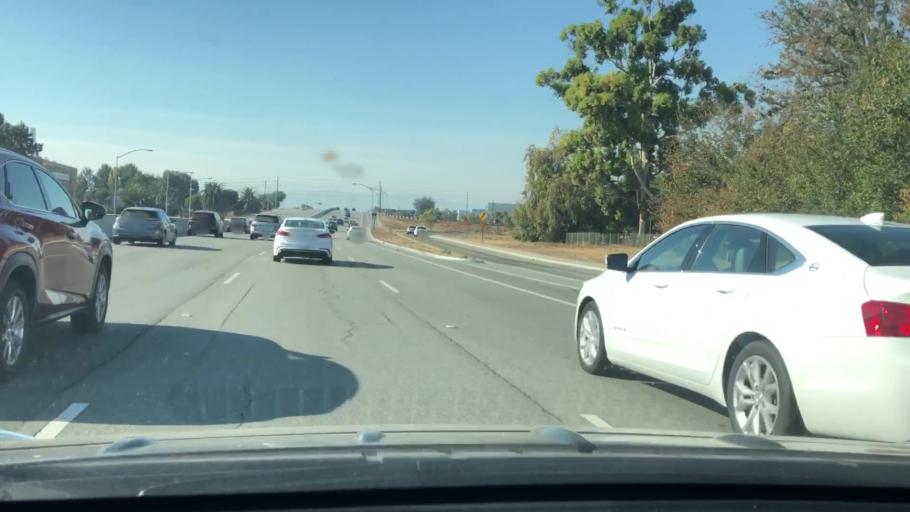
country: US
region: California
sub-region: Santa Clara County
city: Santa Clara
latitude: 37.3917
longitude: -121.9506
